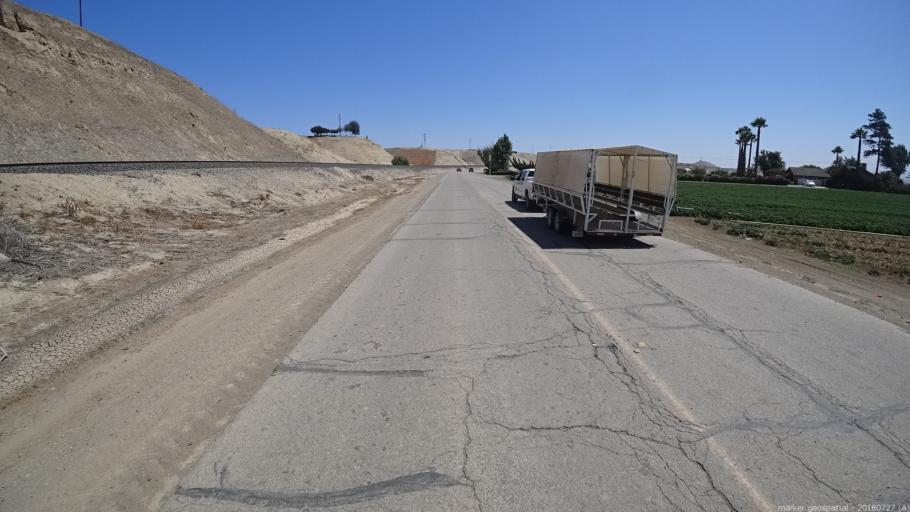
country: US
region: California
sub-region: Monterey County
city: King City
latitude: 36.1874
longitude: -121.0675
